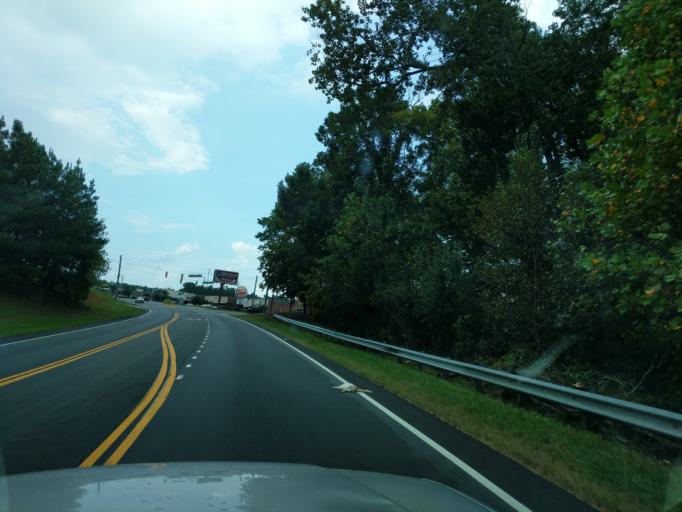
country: US
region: South Carolina
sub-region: Anderson County
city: Northlake
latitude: 34.5732
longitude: -82.6880
